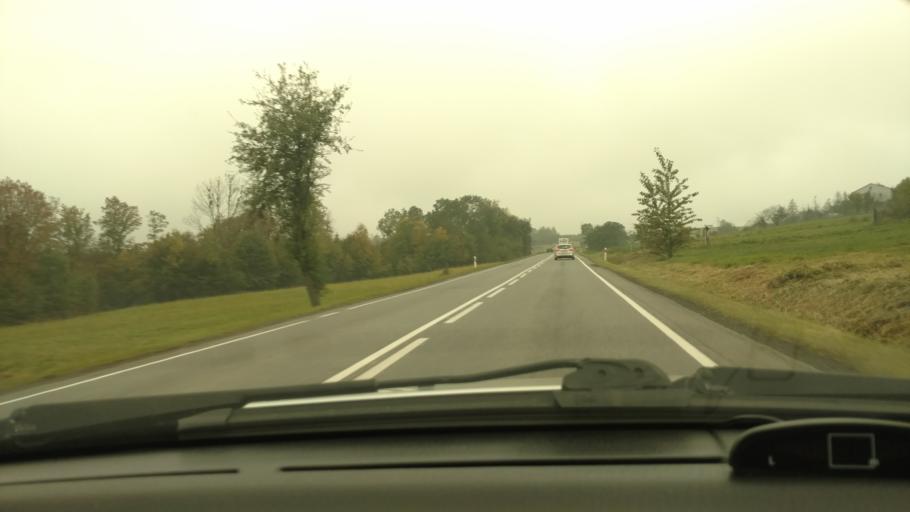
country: PL
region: Lesser Poland Voivodeship
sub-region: Powiat nowosadecki
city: Grybow
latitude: 49.6153
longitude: 20.8886
